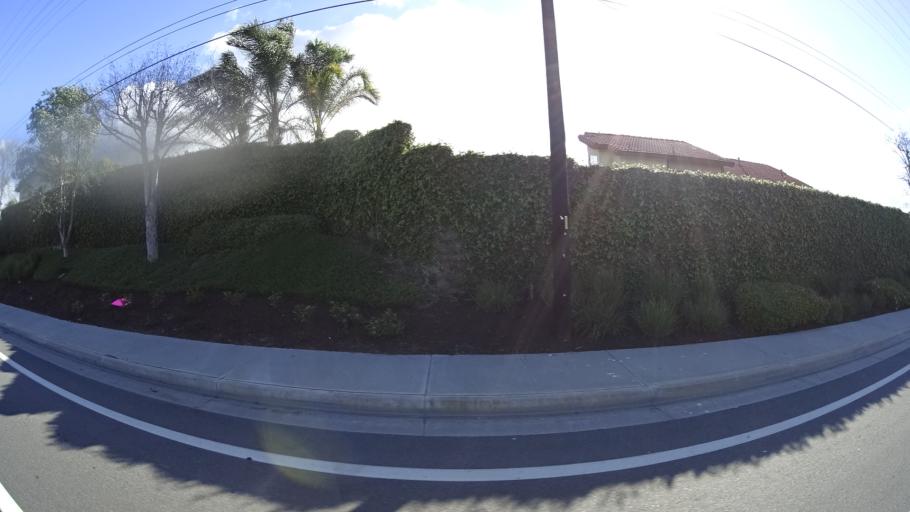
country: US
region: California
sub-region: Riverside County
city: Temecula
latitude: 33.4611
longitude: -117.1100
